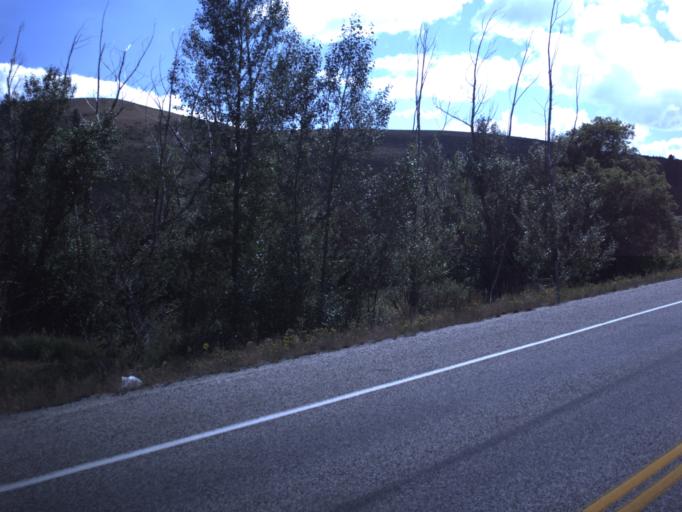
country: US
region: Idaho
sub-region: Bear Lake County
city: Paris
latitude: 41.9292
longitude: -111.4255
